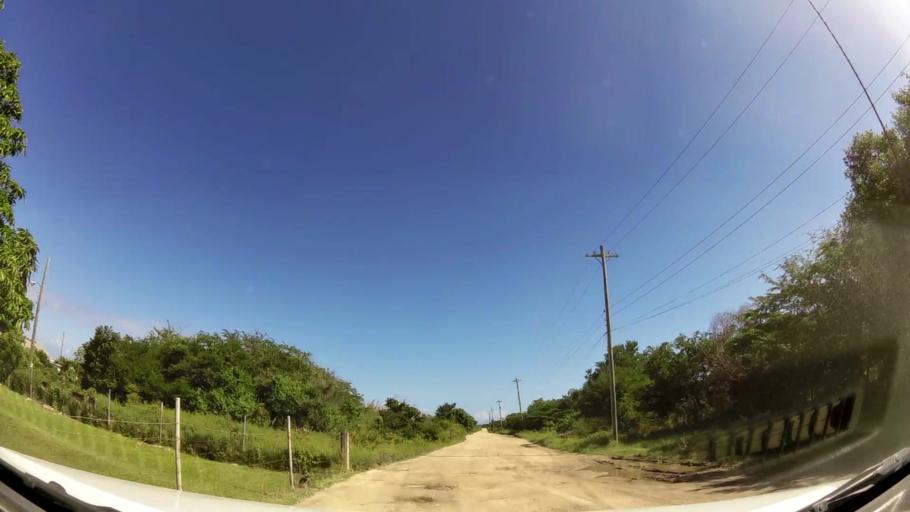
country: AG
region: Barbuda
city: Codrington
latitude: 17.6491
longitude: -61.8183
